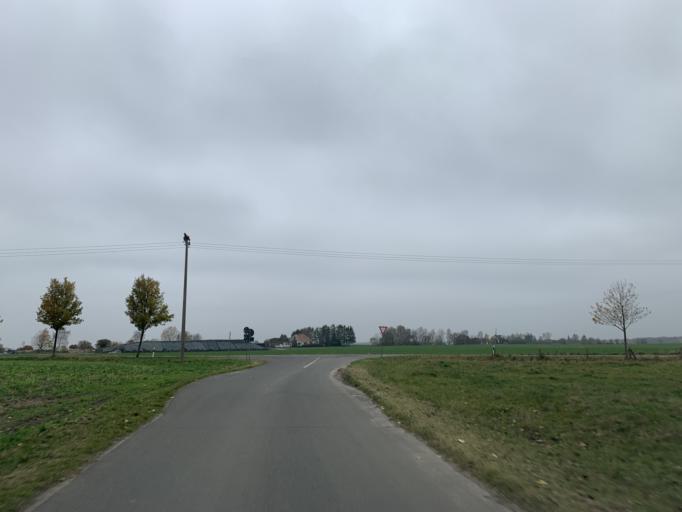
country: DE
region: Mecklenburg-Vorpommern
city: Blankensee
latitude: 53.4113
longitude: 13.2383
